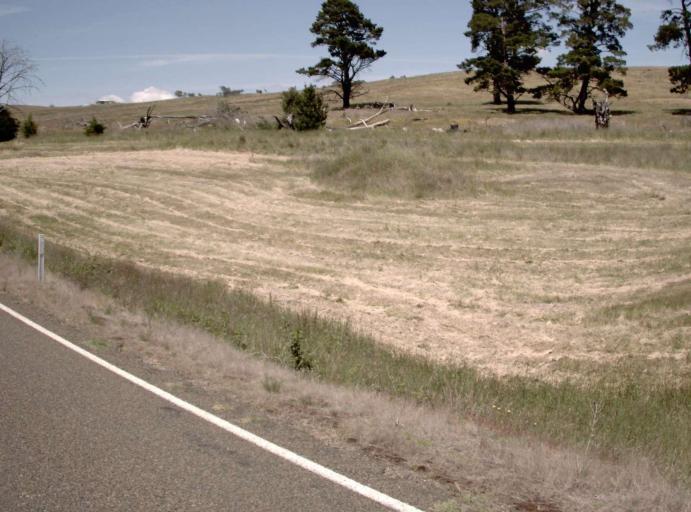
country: AU
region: Victoria
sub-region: Alpine
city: Mount Beauty
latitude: -37.1104
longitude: 147.6079
